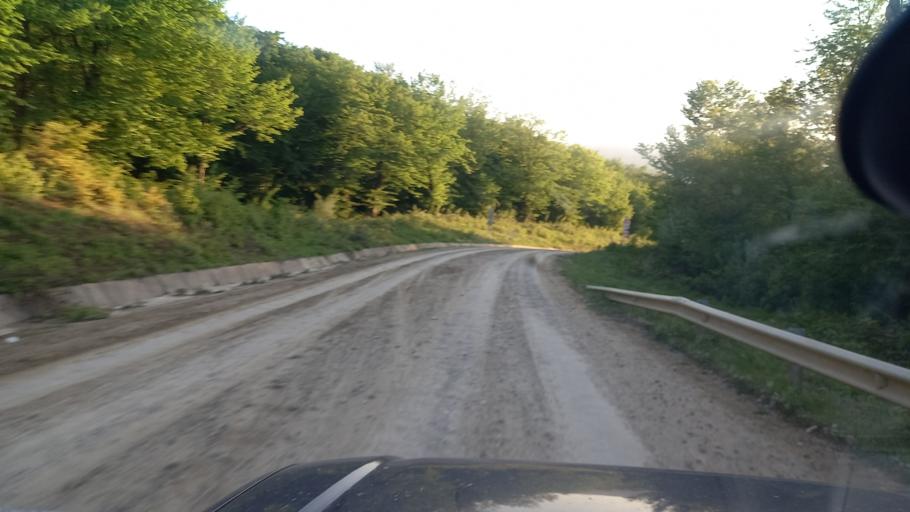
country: RU
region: Dagestan
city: Khuchni
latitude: 42.0041
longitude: 47.9747
